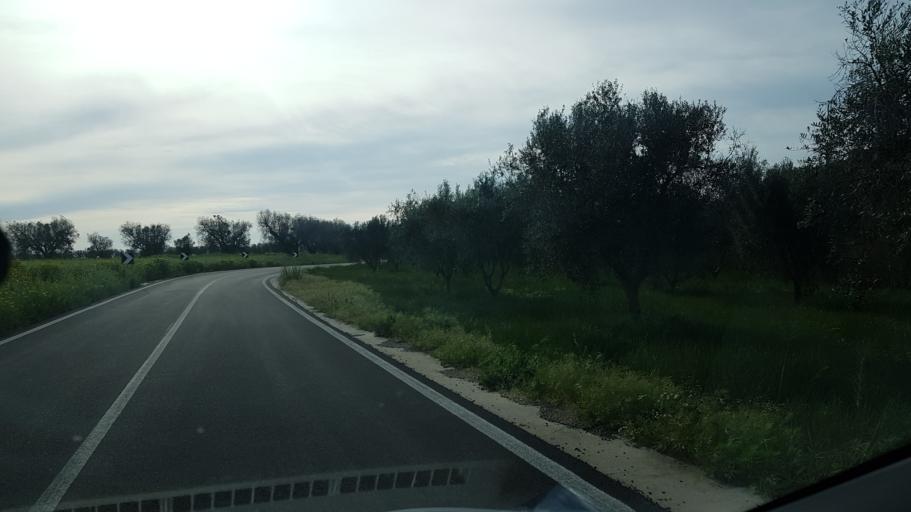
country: IT
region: Apulia
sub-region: Provincia di Brindisi
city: Tuturano
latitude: 40.5242
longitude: 17.9177
